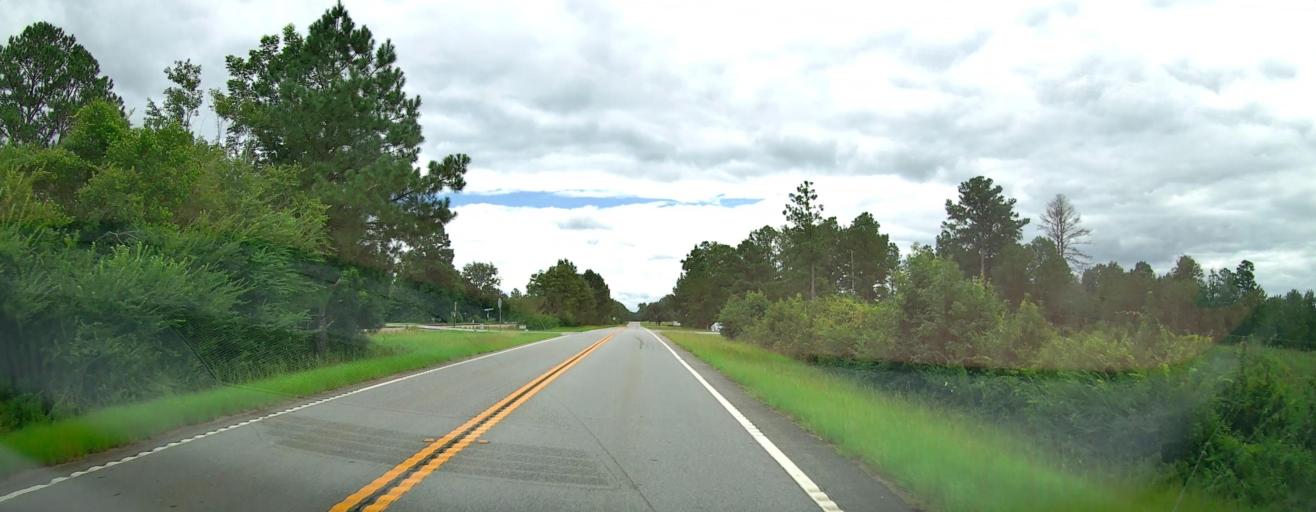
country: US
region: Georgia
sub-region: Twiggs County
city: Jeffersonville
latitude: 32.6683
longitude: -83.3258
